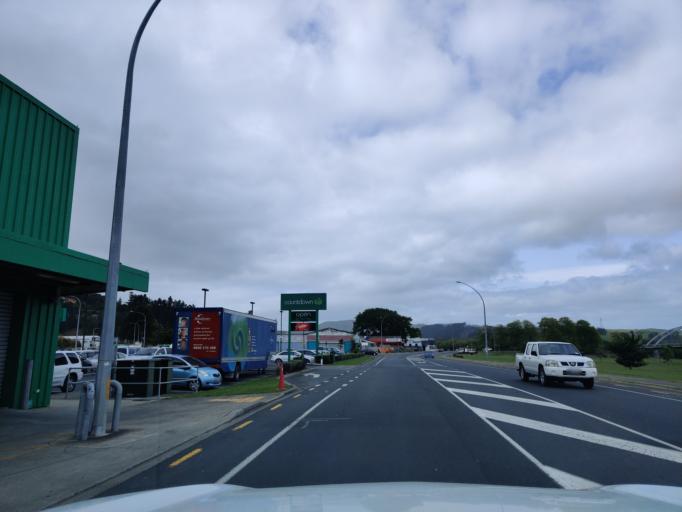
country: NZ
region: Waikato
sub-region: Waikato District
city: Ngaruawahia
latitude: -37.5642
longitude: 175.1584
